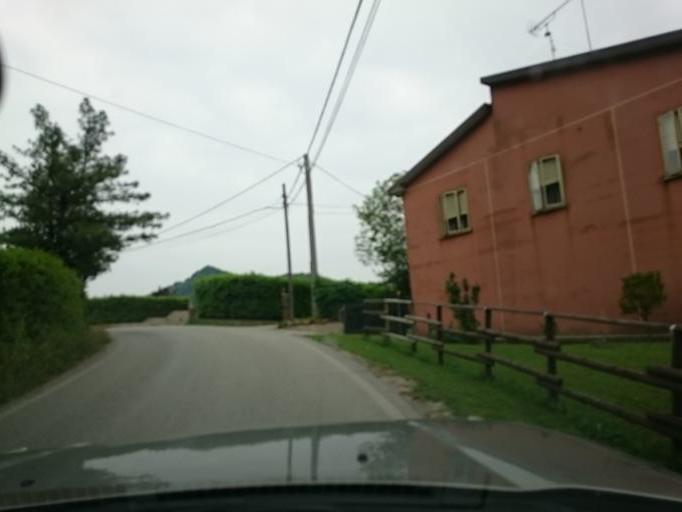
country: IT
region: Veneto
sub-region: Provincia di Padova
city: Montegrotto Terme
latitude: 45.3175
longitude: 11.7610
